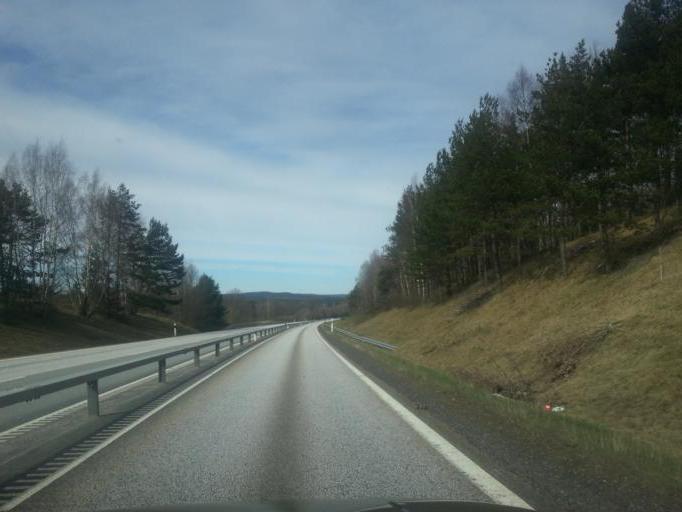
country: SE
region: Joenkoeping
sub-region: Jonkopings Kommun
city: Bankeryd
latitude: 57.8003
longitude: 14.0969
